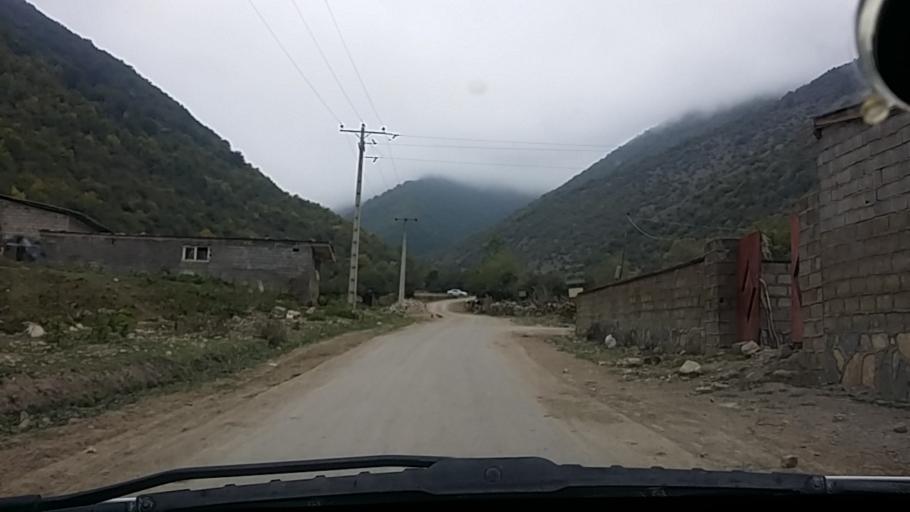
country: IR
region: Mazandaran
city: `Abbasabad
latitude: 36.4645
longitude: 51.1375
